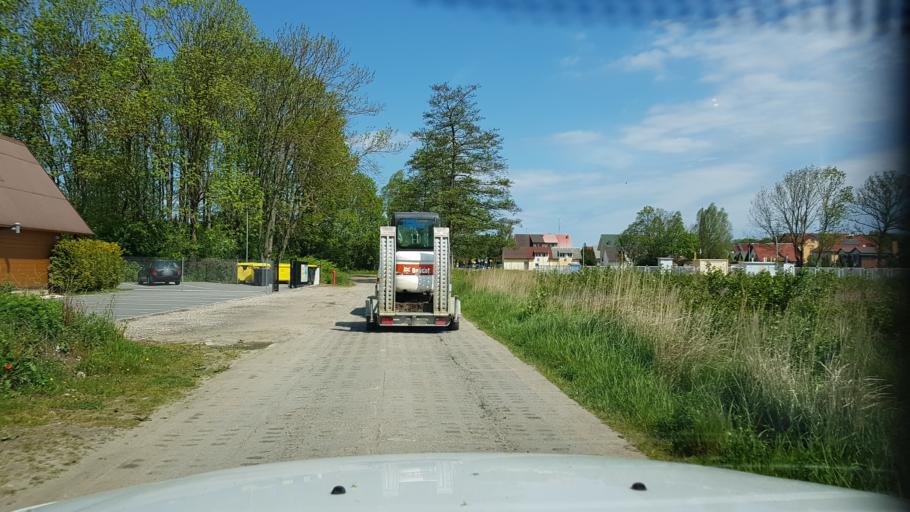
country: PL
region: West Pomeranian Voivodeship
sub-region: Powiat koszalinski
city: Mielno
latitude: 54.2444
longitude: 15.9559
